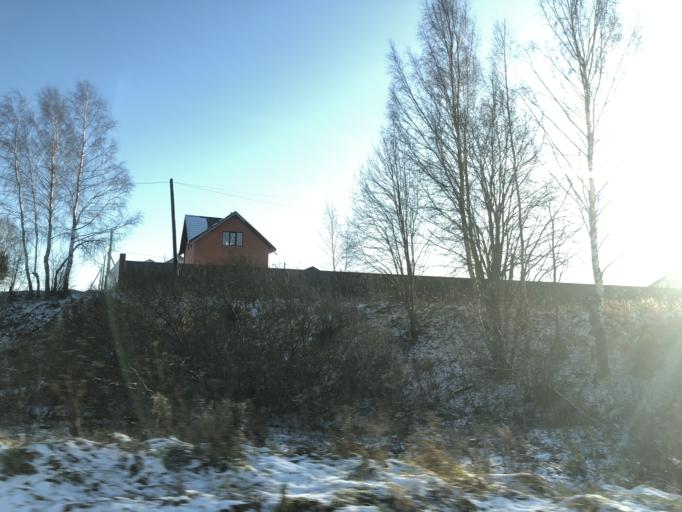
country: RU
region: Tverskaya
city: Rzhev
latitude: 56.2807
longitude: 34.3210
